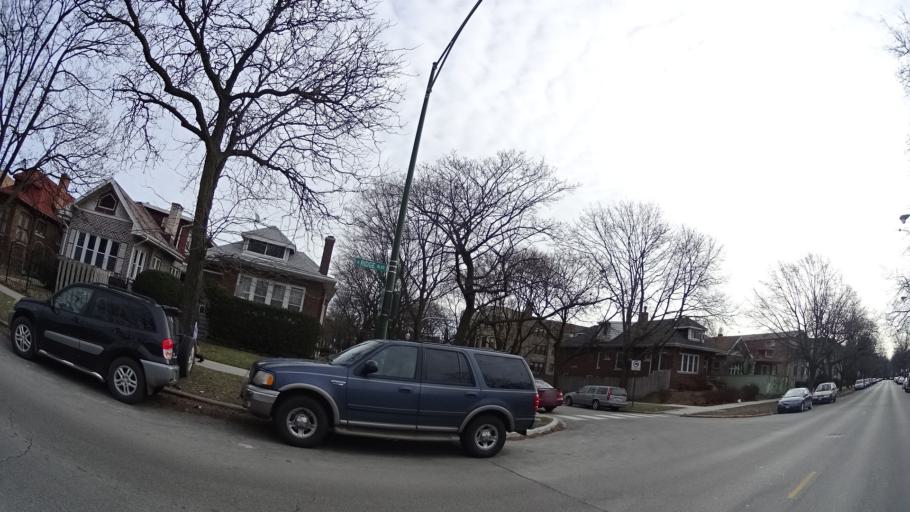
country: US
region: Illinois
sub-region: Cook County
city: Evanston
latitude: 42.0182
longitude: -87.6845
